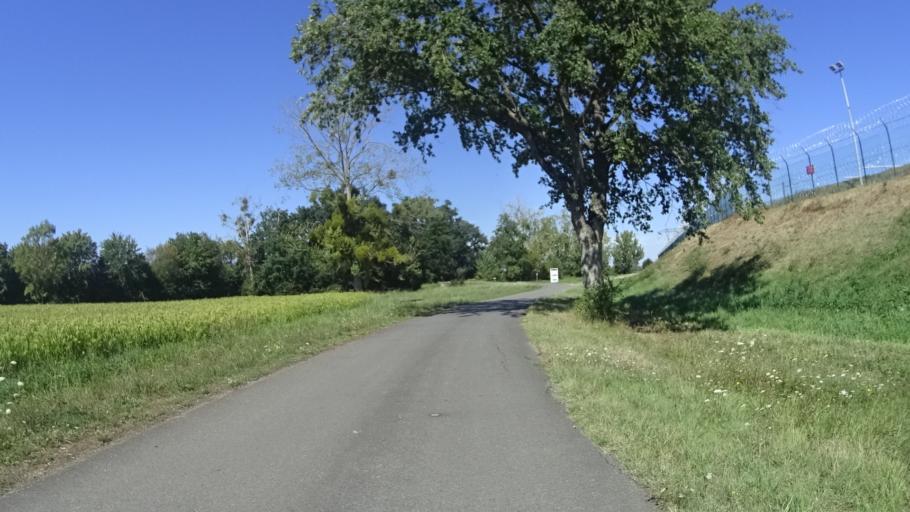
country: FR
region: Centre
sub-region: Departement du Cher
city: Belleville-sur-Loire
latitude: 47.5047
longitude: 2.8700
